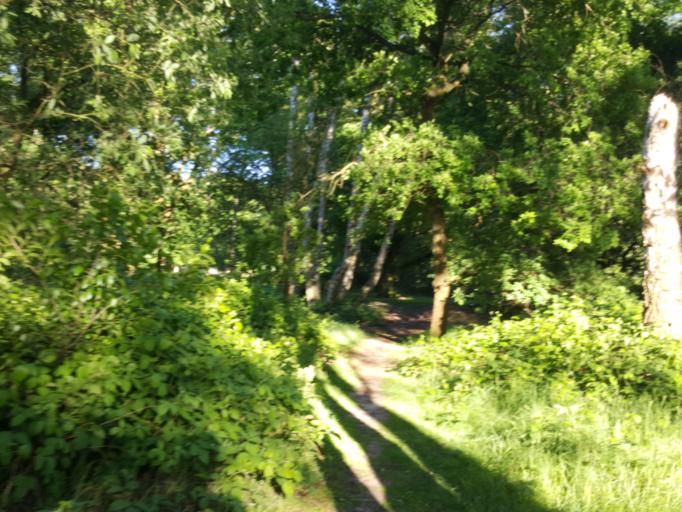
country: DE
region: Schleswig-Holstein
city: Oststeinbek
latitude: 53.5169
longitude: 10.1457
